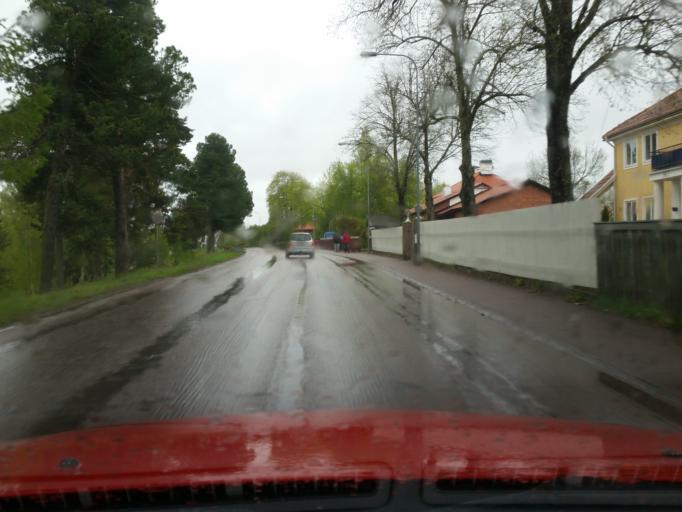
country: SE
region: Dalarna
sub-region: Hedemora Kommun
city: Hedemora
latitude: 60.2843
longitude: 15.9770
